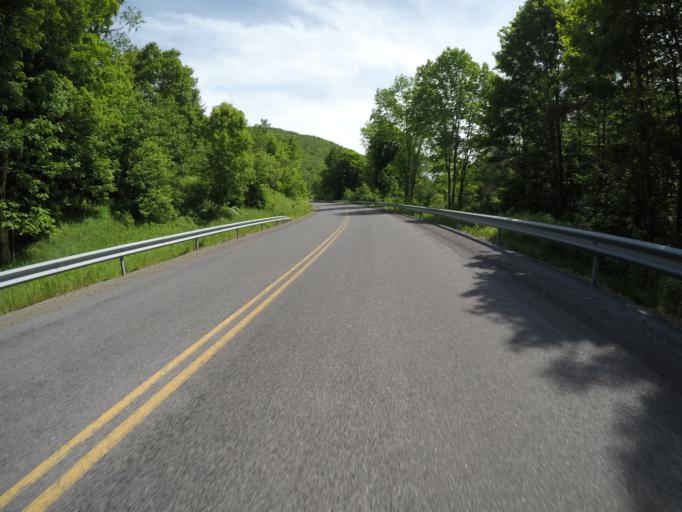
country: US
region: New York
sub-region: Delaware County
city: Delhi
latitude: 42.1188
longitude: -74.8207
